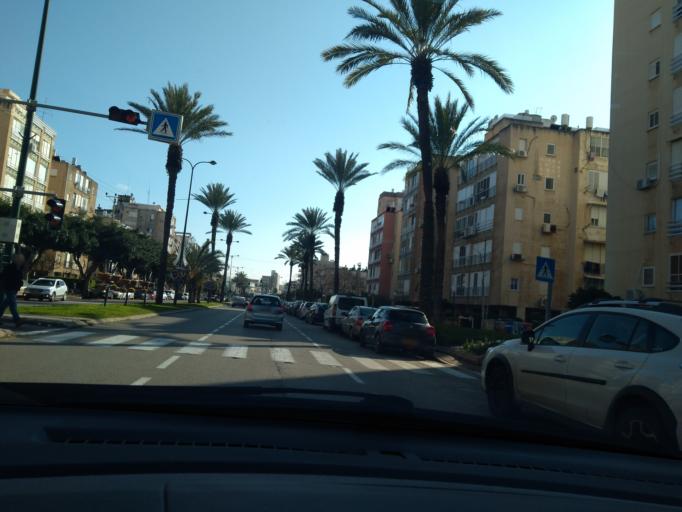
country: IL
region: Central District
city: Netanya
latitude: 32.3331
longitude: 34.8591
